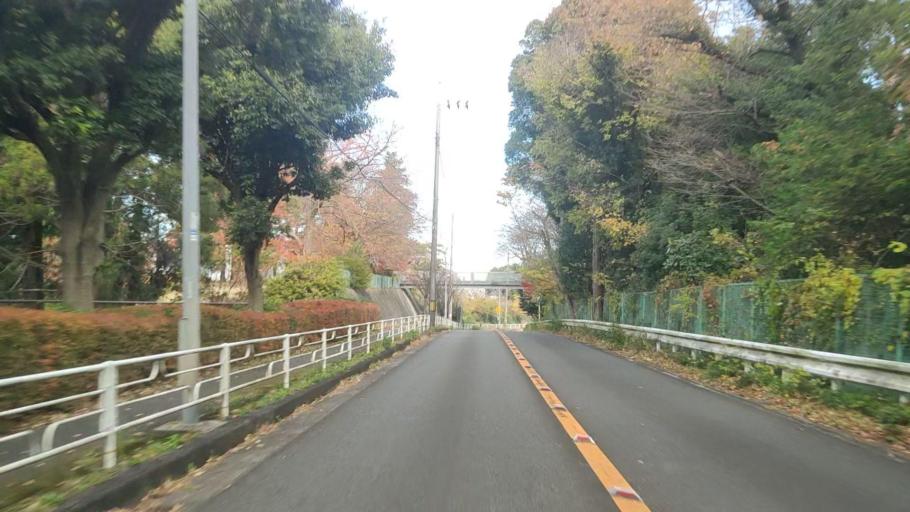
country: JP
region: Kanagawa
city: Minami-rinkan
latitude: 35.4494
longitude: 139.5384
